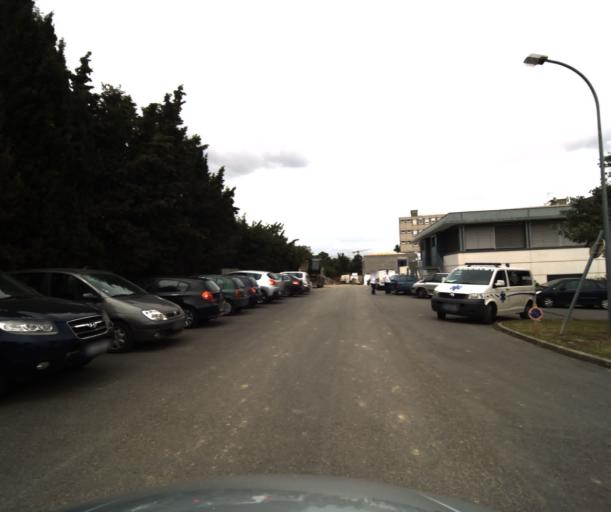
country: FR
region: Midi-Pyrenees
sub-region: Departement de la Haute-Garonne
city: Muret
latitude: 43.4646
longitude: 1.3388
